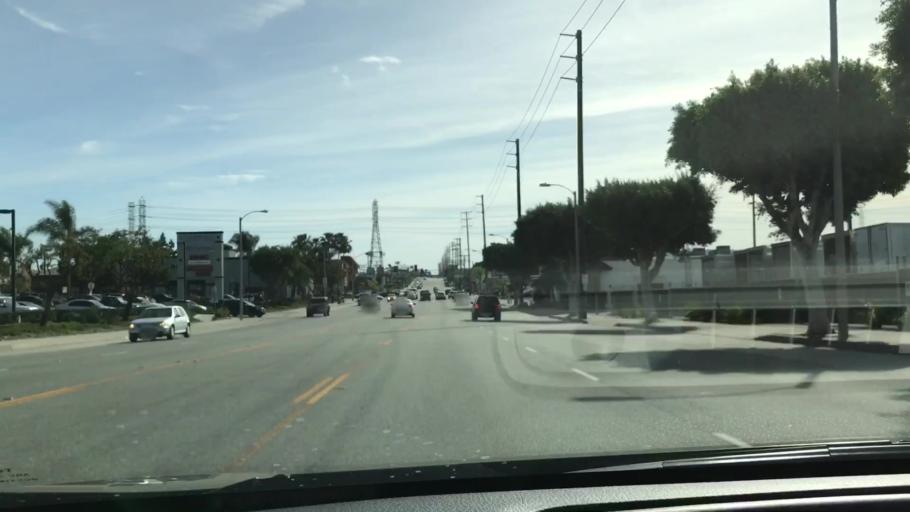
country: US
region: California
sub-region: Los Angeles County
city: Gardena
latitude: 33.8747
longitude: -118.3092
